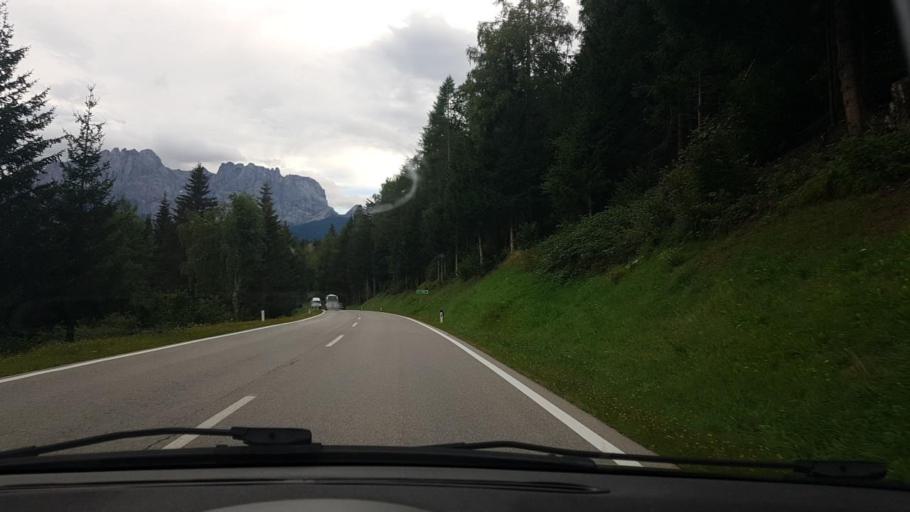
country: AT
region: Tyrol
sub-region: Politischer Bezirk Lienz
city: Dolsach
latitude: 46.8501
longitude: 12.8542
